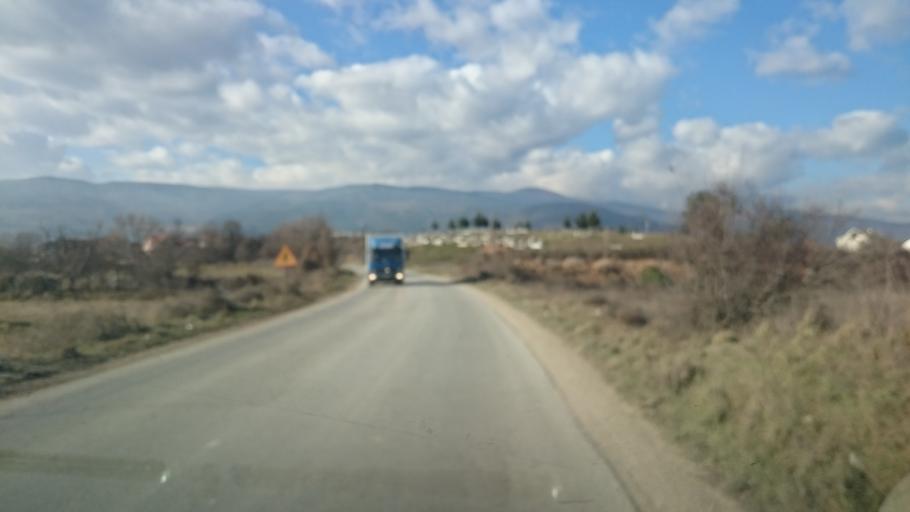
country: MK
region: Kicevo
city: Kicevo
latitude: 41.4991
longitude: 20.9607
